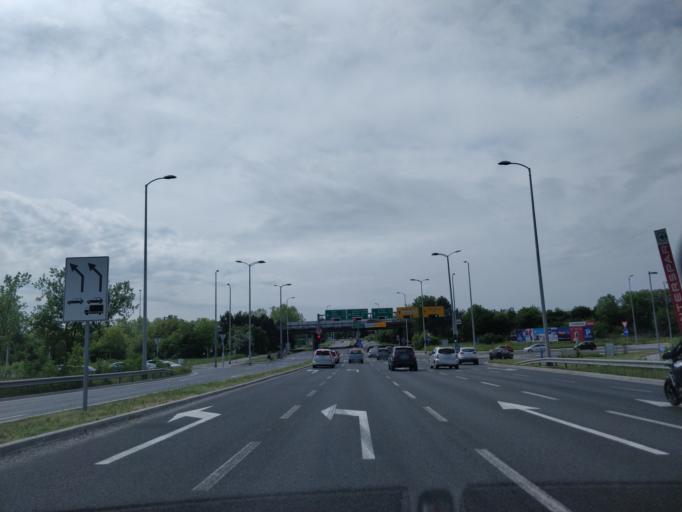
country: HR
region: Grad Zagreb
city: Odra
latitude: 45.7551
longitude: 15.9894
